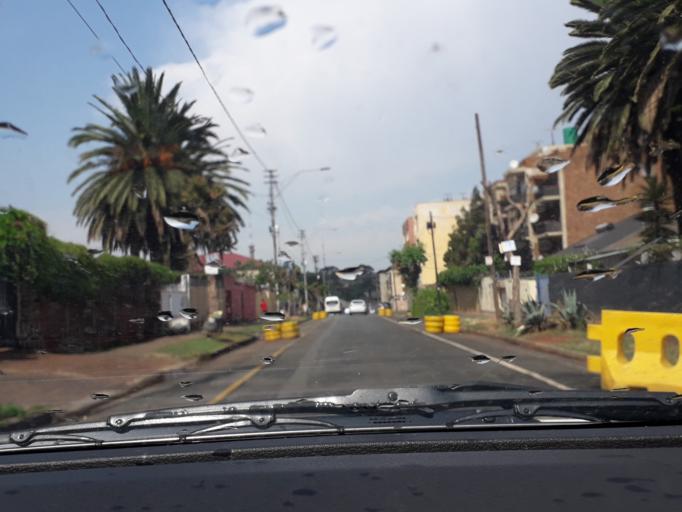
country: ZA
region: Gauteng
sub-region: City of Johannesburg Metropolitan Municipality
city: Johannesburg
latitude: -26.1855
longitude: 28.0681
